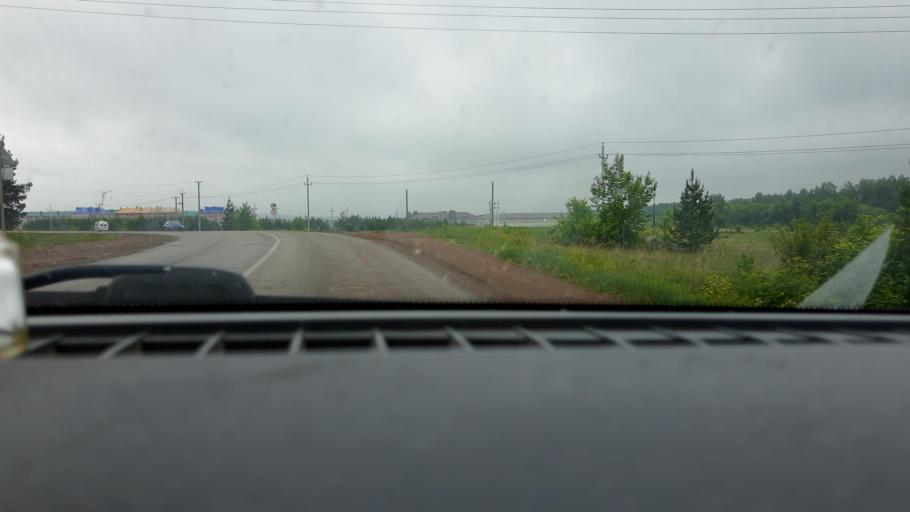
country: RU
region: Bashkortostan
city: Belebey
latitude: 54.0834
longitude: 54.0921
